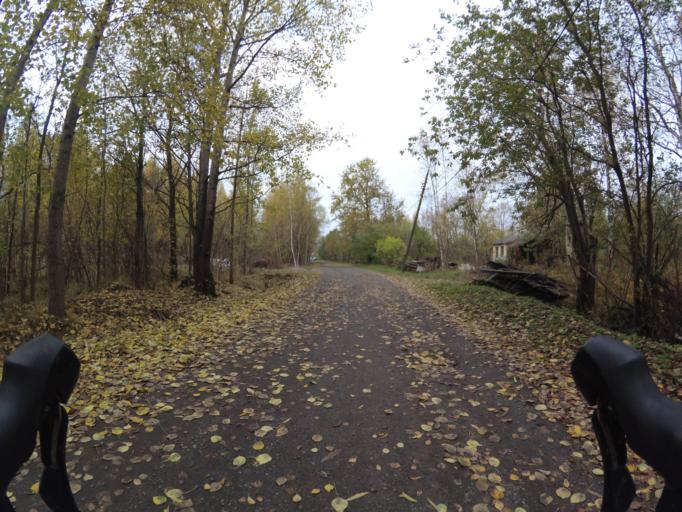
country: RU
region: St.-Petersburg
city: Lakhtinskiy
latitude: 59.9968
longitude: 30.1625
